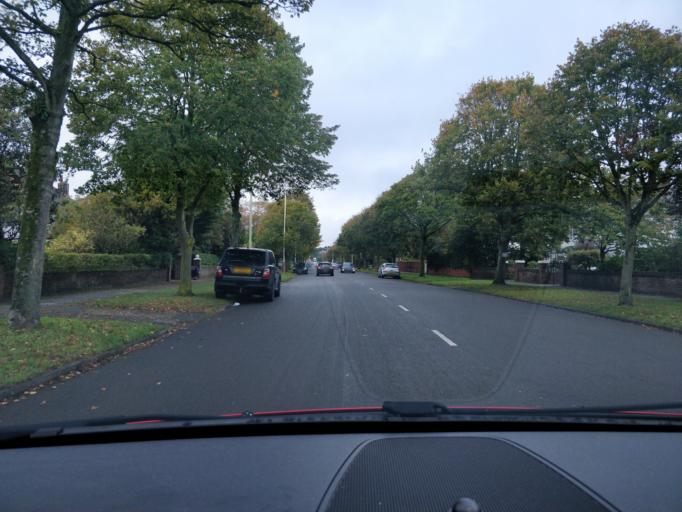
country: GB
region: England
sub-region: Sefton
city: Southport
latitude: 53.6160
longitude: -3.0207
